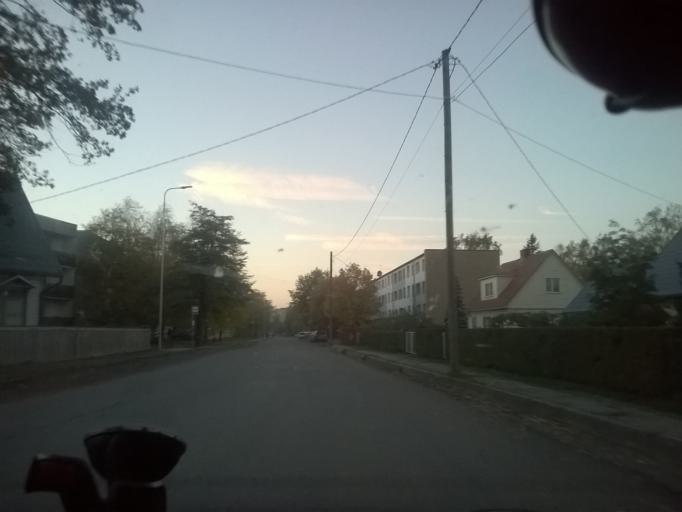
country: EE
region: Laeaene
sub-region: Haapsalu linn
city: Haapsalu
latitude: 58.9398
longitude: 23.5523
